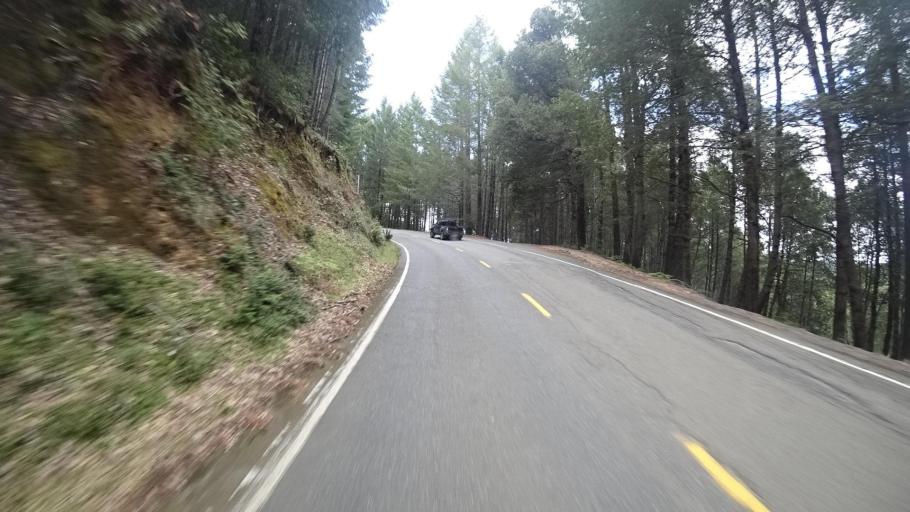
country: US
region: California
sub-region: Humboldt County
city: Redway
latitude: 40.0556
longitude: -123.9915
